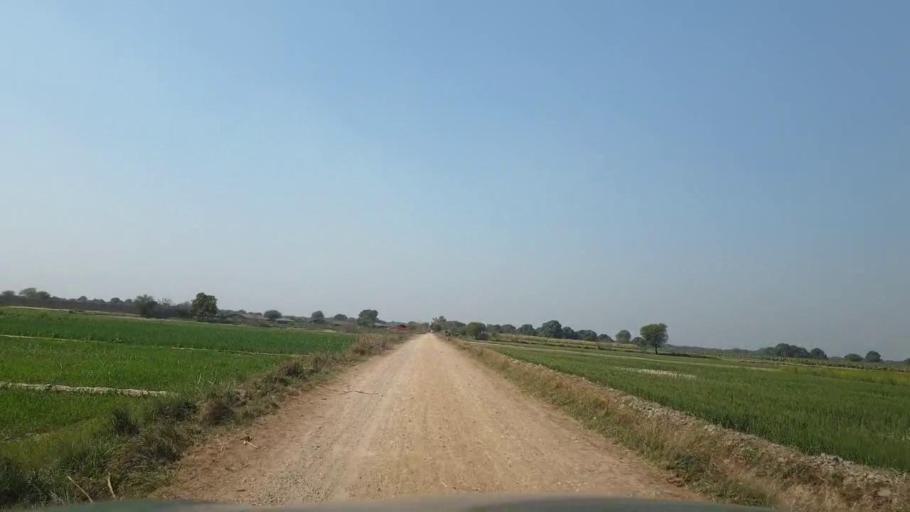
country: PK
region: Sindh
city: Tando Allahyar
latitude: 25.5558
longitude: 68.6821
